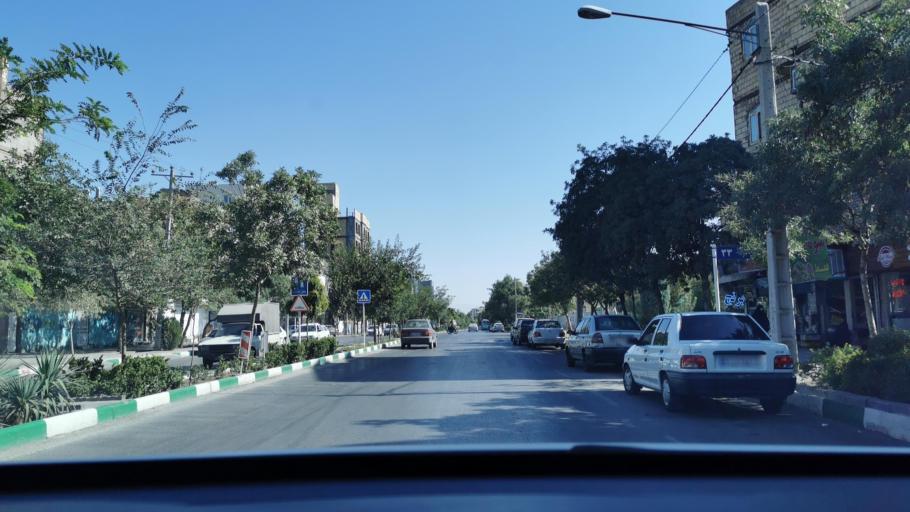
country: IR
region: Razavi Khorasan
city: Mashhad
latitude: 36.3326
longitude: 59.5915
